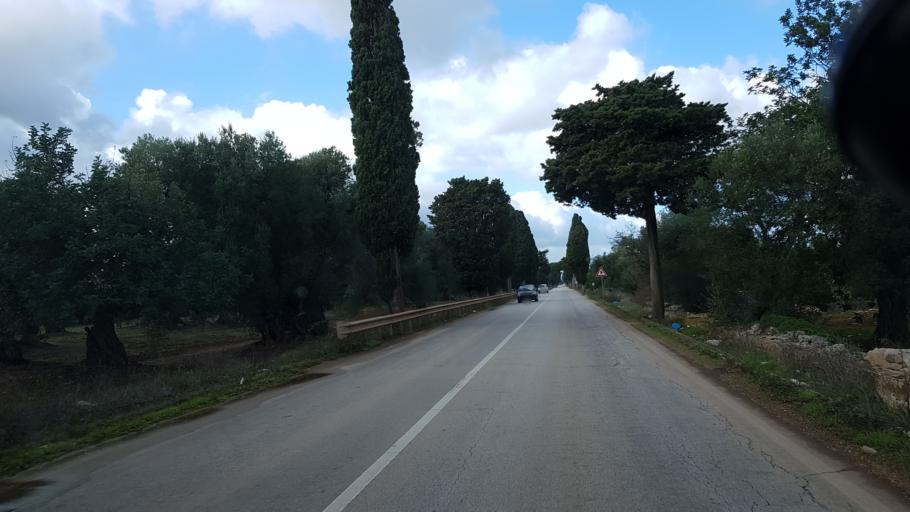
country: IT
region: Apulia
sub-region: Provincia di Brindisi
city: Montalbano
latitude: 40.7668
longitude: 17.5149
